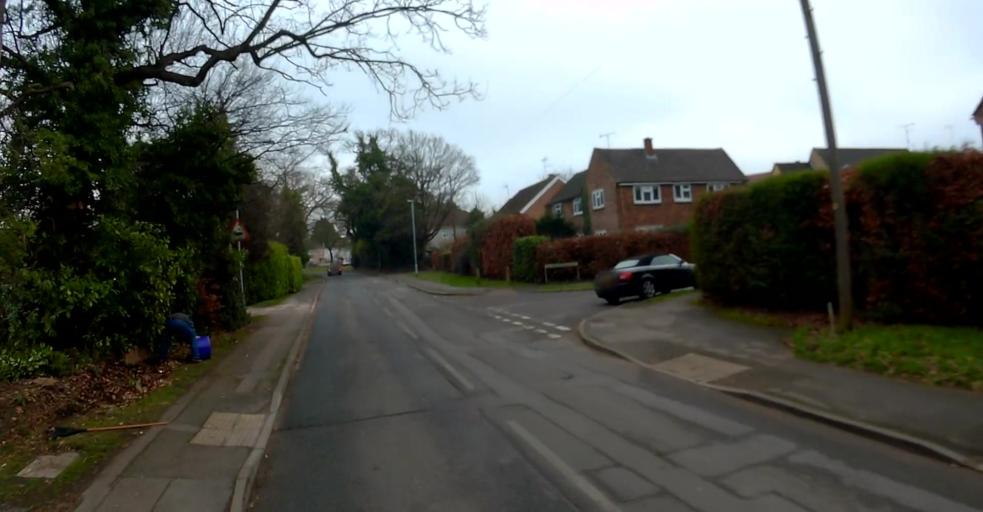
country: GB
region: England
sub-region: Wokingham
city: Wokingham
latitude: 51.4060
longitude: -0.8171
